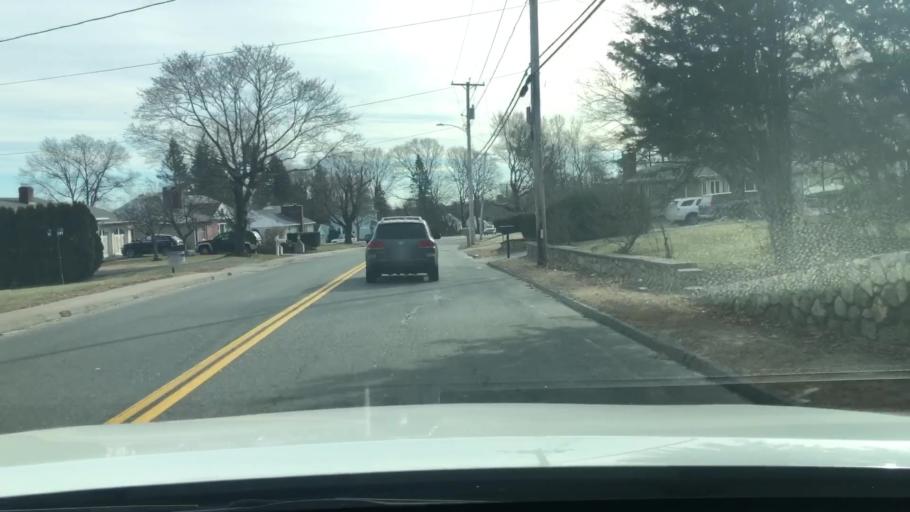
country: US
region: Massachusetts
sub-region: Worcester County
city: Hopedale
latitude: 42.1444
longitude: -71.5371
